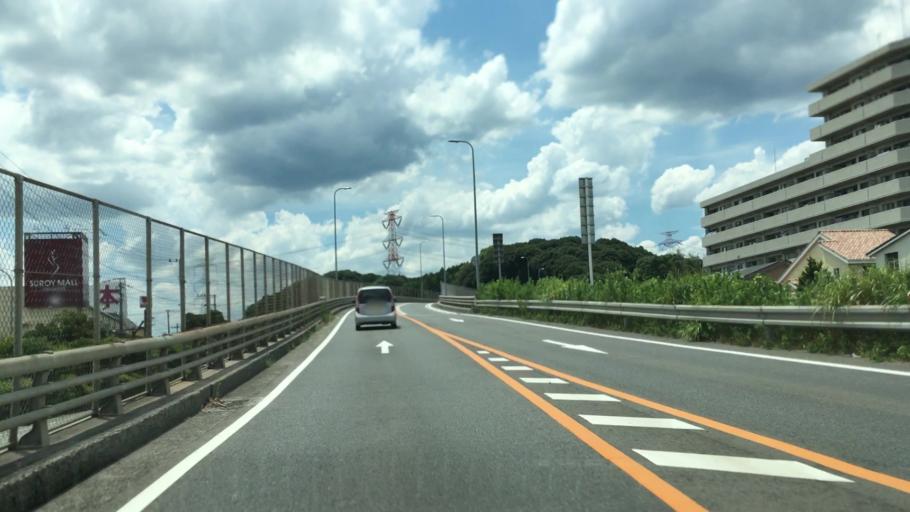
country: JP
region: Fukuoka
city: Chikushino-shi
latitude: 33.4456
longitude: 130.5384
